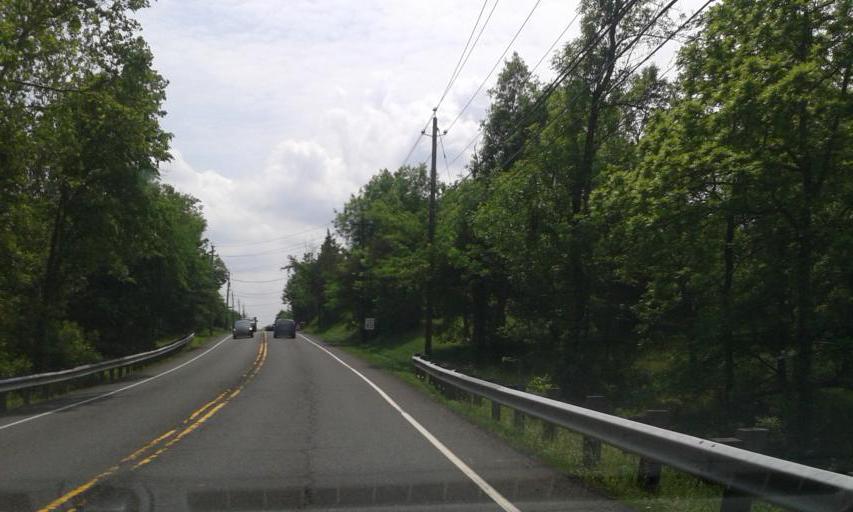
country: US
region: New Jersey
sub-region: Hunterdon County
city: Whitehouse Station
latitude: 40.6307
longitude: -74.7671
